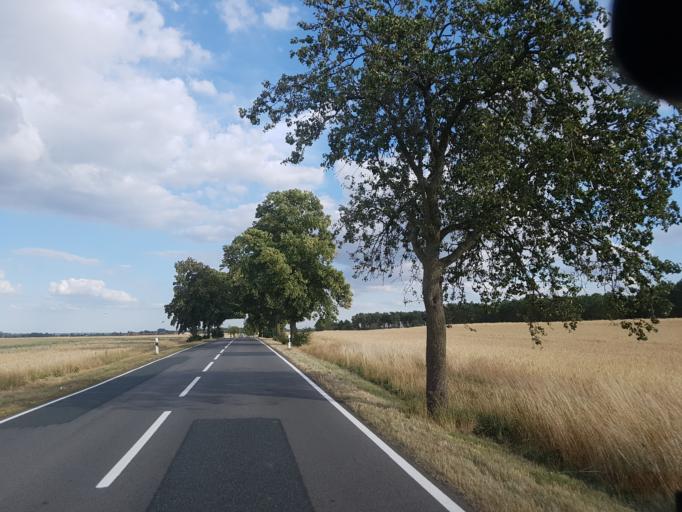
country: DE
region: Brandenburg
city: Schlieben
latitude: 51.7384
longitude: 13.2989
